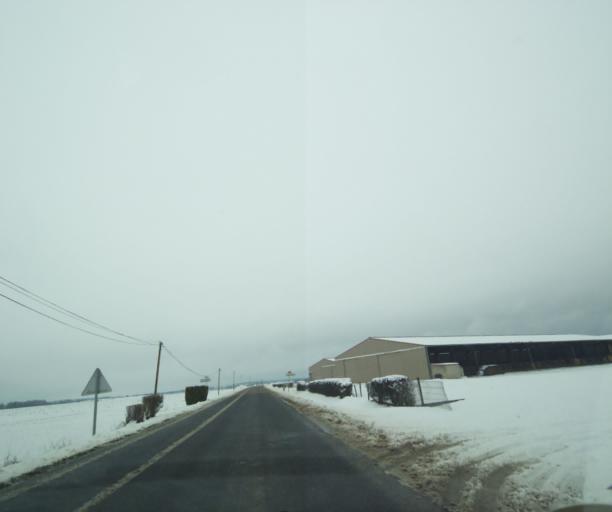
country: FR
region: Champagne-Ardenne
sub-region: Departement de la Haute-Marne
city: Montier-en-Der
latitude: 48.4434
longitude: 4.8025
